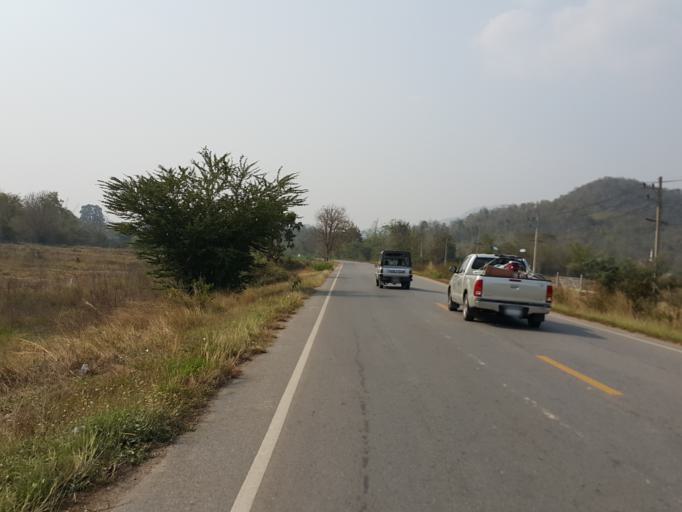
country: TH
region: Sukhothai
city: Thung Saliam
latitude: 17.3333
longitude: 99.4957
